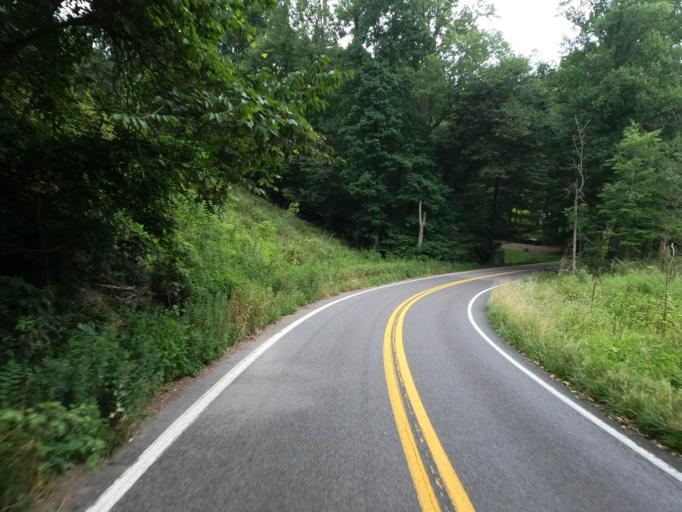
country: US
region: West Virginia
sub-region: Marion County
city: Fairmont
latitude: 39.5001
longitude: -80.0982
